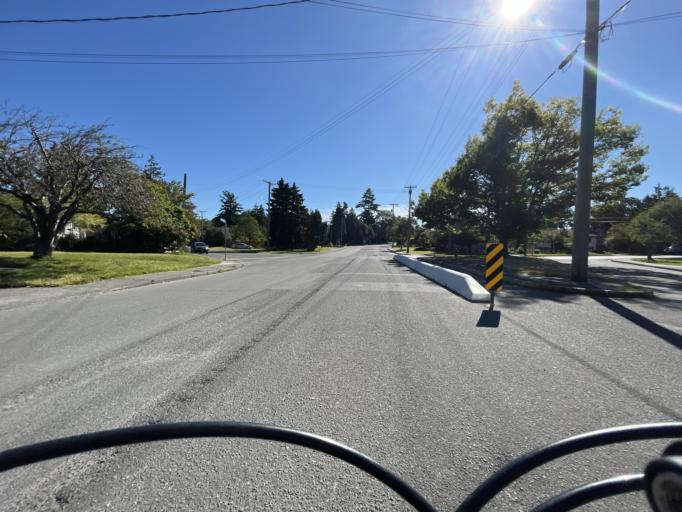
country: CA
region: British Columbia
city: Oak Bay
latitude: 48.4200
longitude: -123.3258
